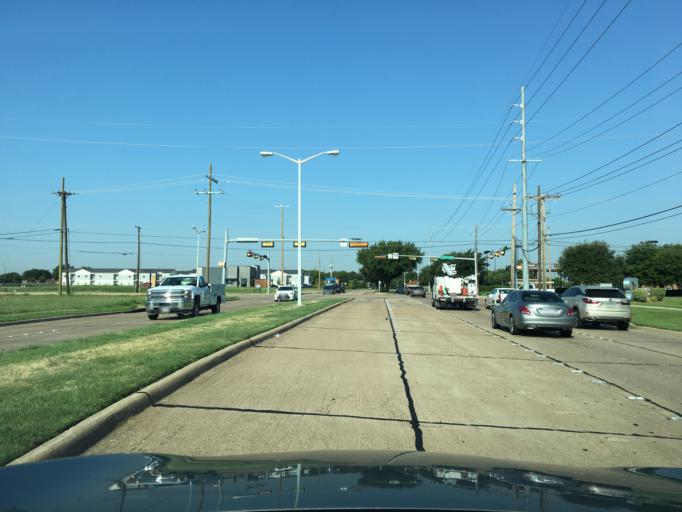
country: US
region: Texas
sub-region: Dallas County
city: Garland
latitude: 32.9595
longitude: -96.6644
